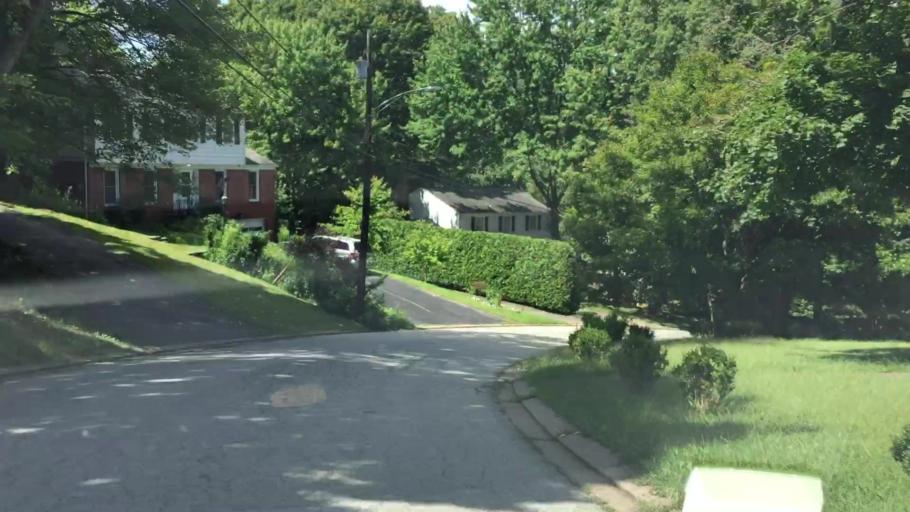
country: US
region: Pennsylvania
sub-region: Allegheny County
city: Bethel Park
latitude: 40.3133
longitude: -80.0601
